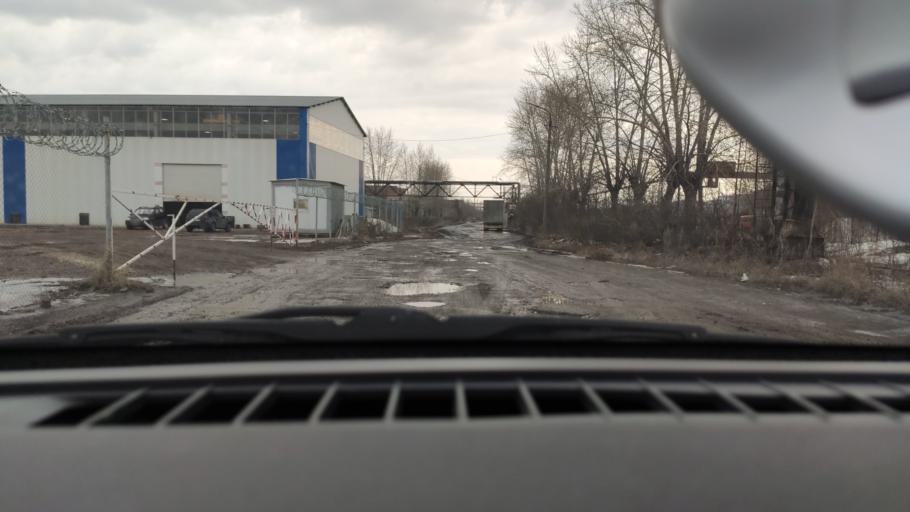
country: RU
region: Perm
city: Perm
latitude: 58.0454
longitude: 56.3141
